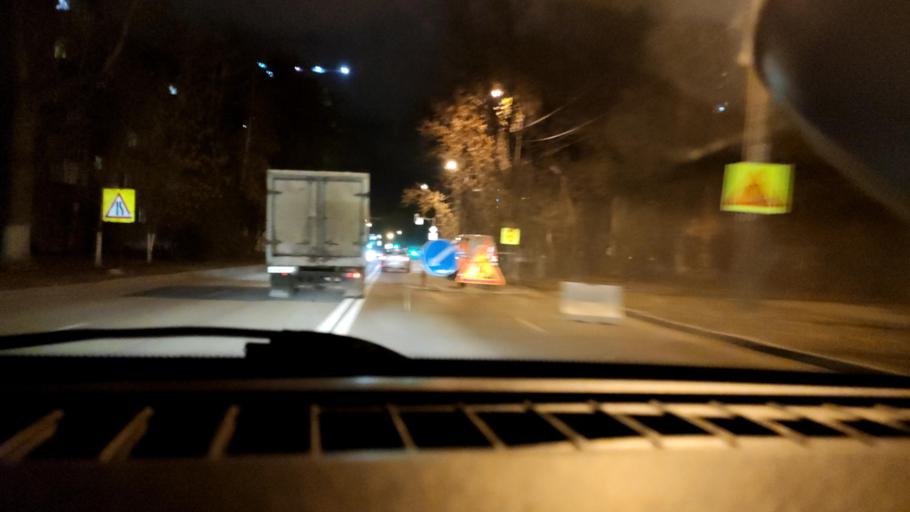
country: RU
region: Samara
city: Samara
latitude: 53.2026
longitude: 50.1784
